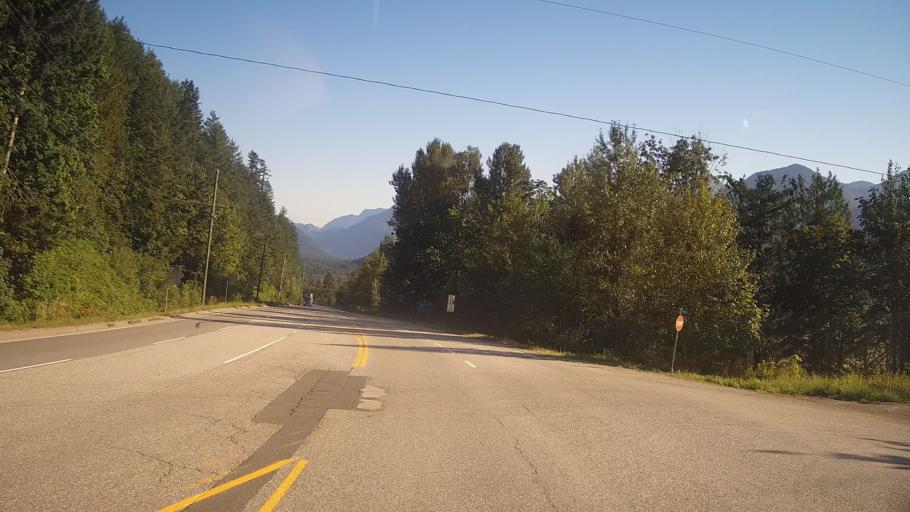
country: CA
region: British Columbia
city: Hope
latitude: 49.4155
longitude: -121.4376
